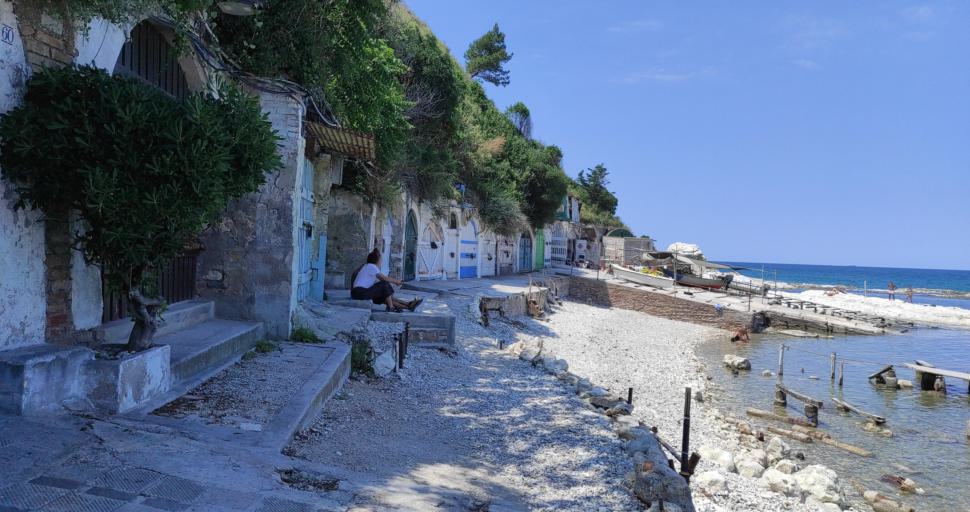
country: IT
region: The Marches
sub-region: Provincia di Ancona
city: Pietra la Croce
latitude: 43.6184
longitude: 13.5317
